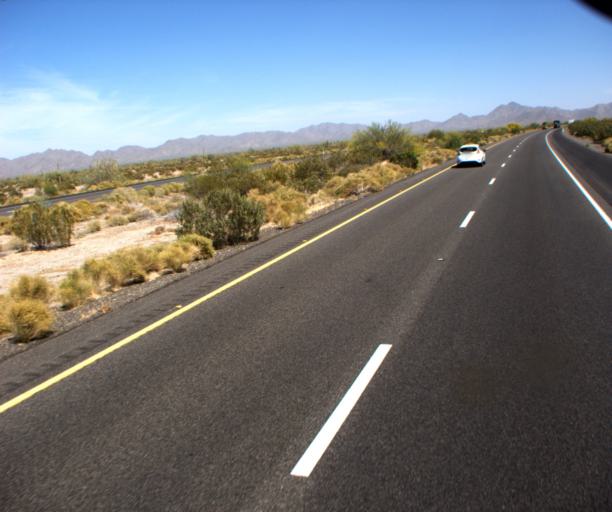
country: US
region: Arizona
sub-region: Maricopa County
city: Gila Bend
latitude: 32.9073
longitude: -112.5427
